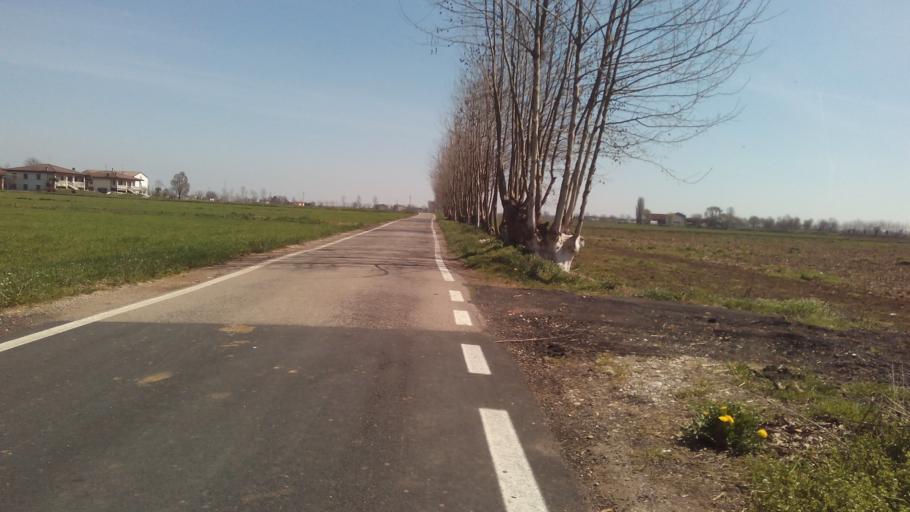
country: IT
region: Lombardy
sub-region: Provincia di Mantova
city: Cerlongo
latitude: 45.2859
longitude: 10.6738
